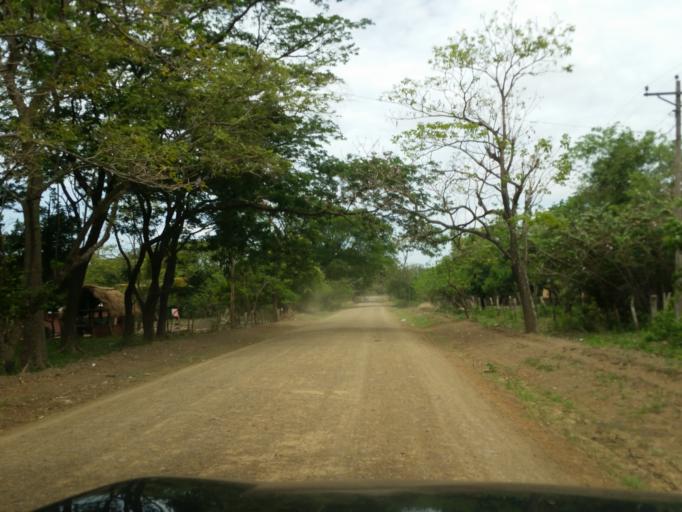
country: NI
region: Granada
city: Nandaime
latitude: 11.6351
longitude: -86.0102
